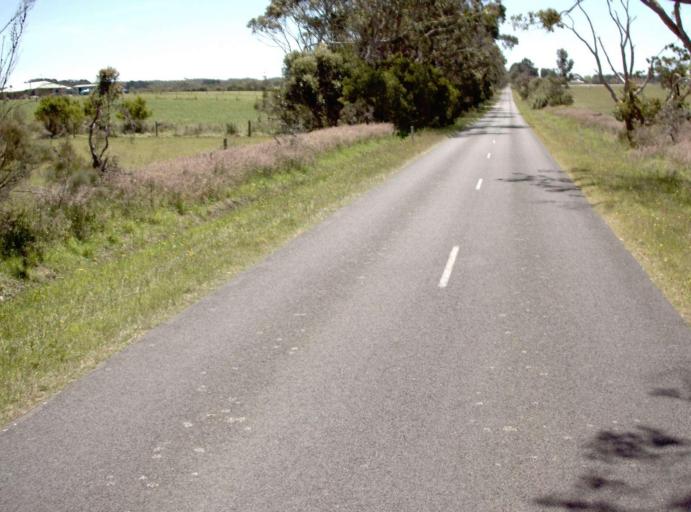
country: AU
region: Victoria
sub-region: Bass Coast
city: North Wonthaggi
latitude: -38.7838
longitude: 146.0826
